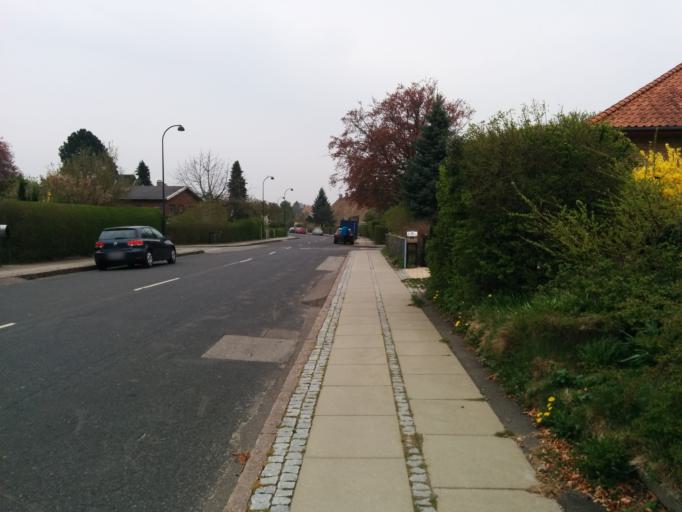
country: DK
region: Capital Region
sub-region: Lyngby-Tarbaek Kommune
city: Kongens Lyngby
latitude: 55.7305
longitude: 12.5283
